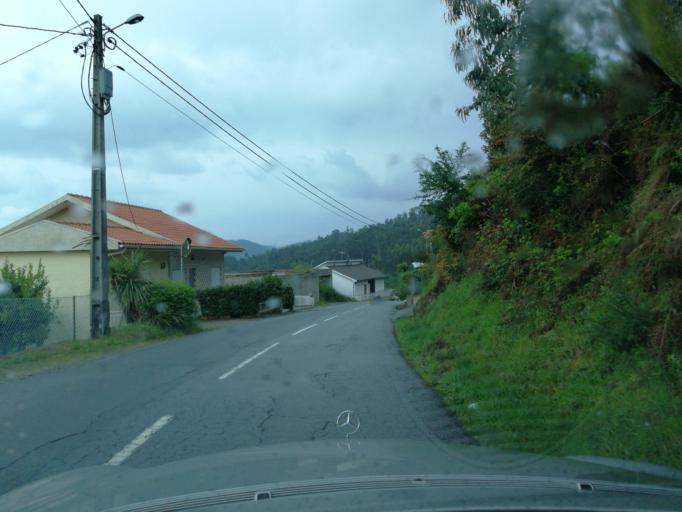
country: PT
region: Braga
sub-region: Vila Nova de Famalicao
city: Joane
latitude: 41.4753
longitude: -8.4278
